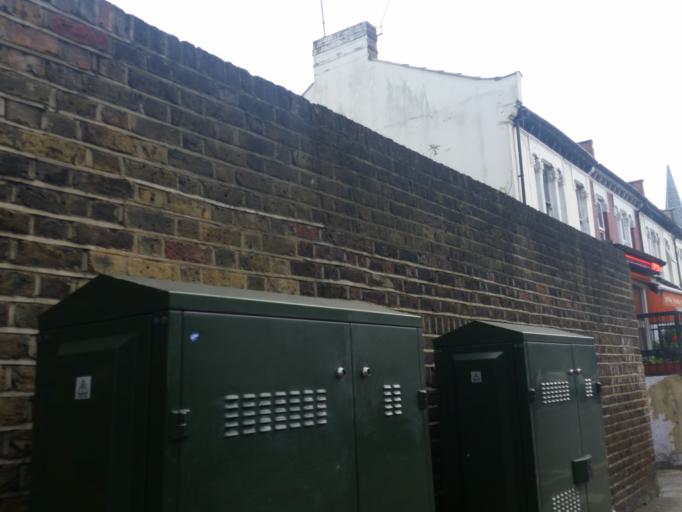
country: GB
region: England
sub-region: Greater London
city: Harringay
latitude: 51.5870
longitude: -0.1085
